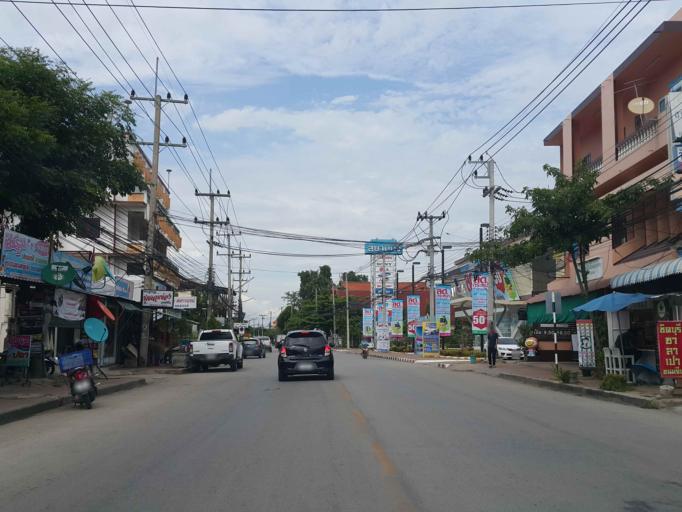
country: TH
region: Lamphun
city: Lamphun
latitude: 18.5931
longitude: 99.0142
